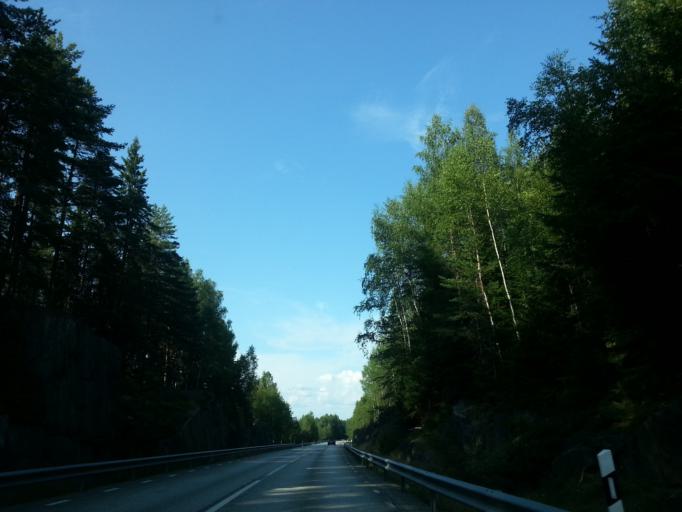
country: SE
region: Vaestmanland
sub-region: Skinnskattebergs Kommun
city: Skinnskatteberg
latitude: 59.8579
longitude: 15.5898
